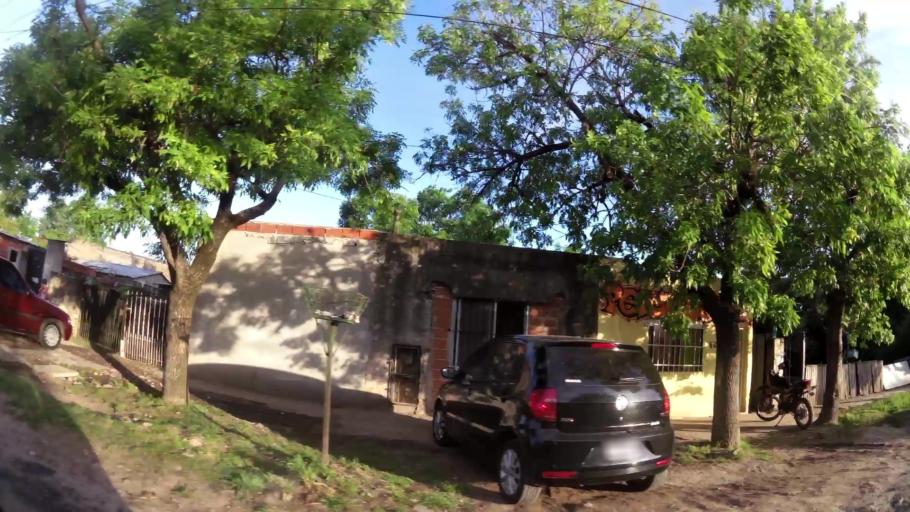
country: AR
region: Buenos Aires
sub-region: Partido de Quilmes
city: Quilmes
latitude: -34.7941
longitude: -58.1924
